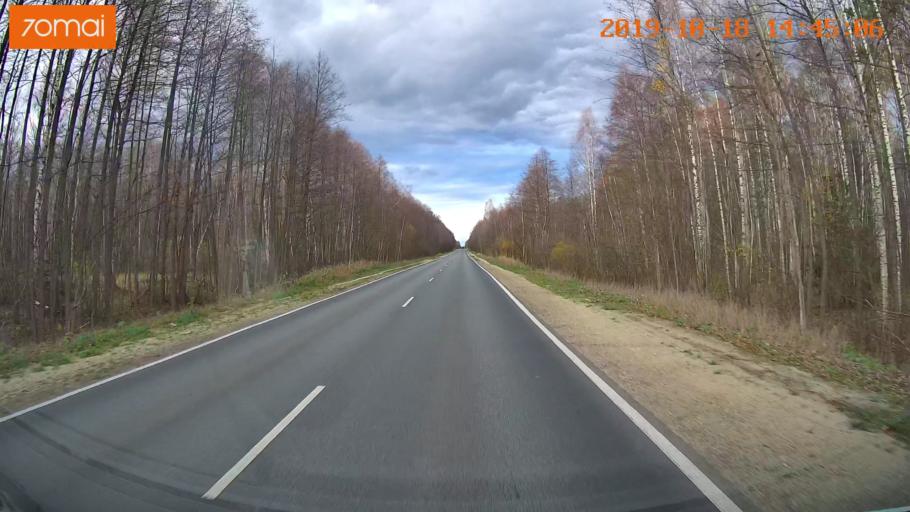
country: RU
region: Vladimir
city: Velikodvorskiy
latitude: 55.3493
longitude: 40.6782
